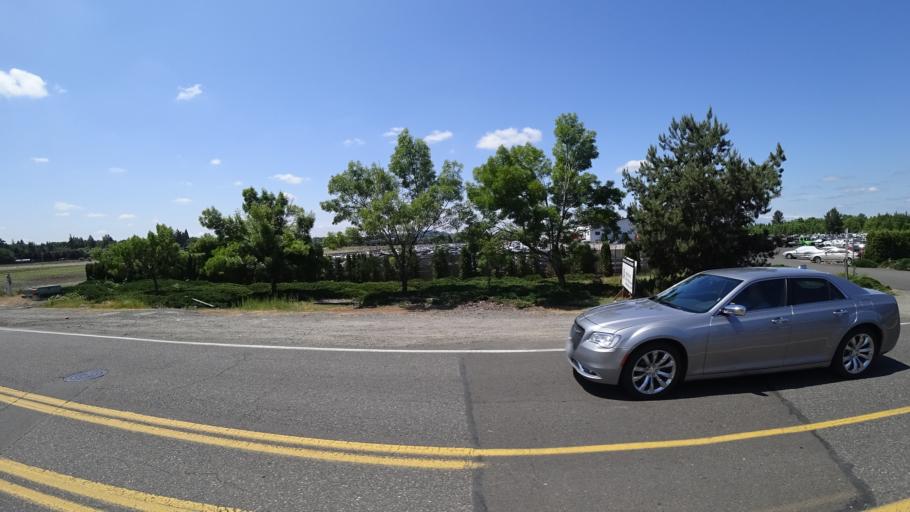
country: US
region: Oregon
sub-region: Multnomah County
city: Fairview
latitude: 45.5547
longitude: -122.5002
